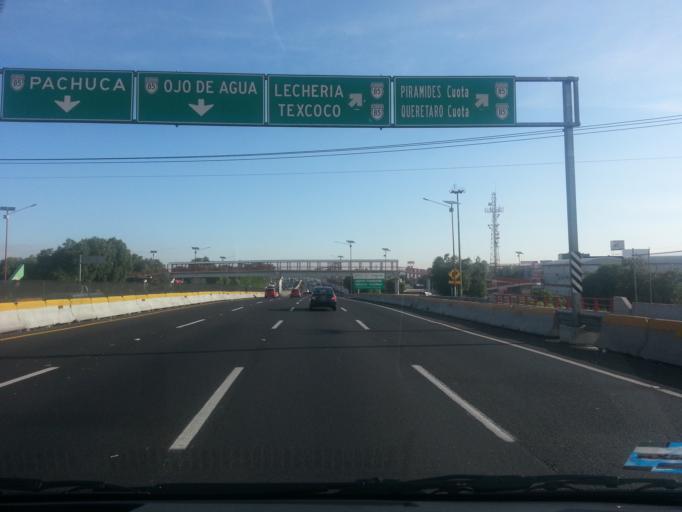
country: MX
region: Mexico
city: Ecatepec
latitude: 19.5895
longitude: -99.0415
